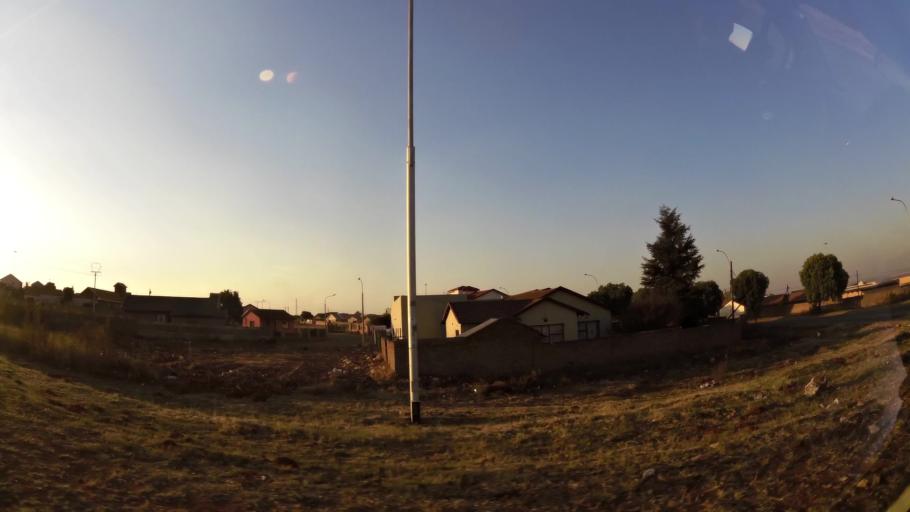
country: ZA
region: Gauteng
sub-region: West Rand District Municipality
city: Randfontein
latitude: -26.2117
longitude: 27.7071
